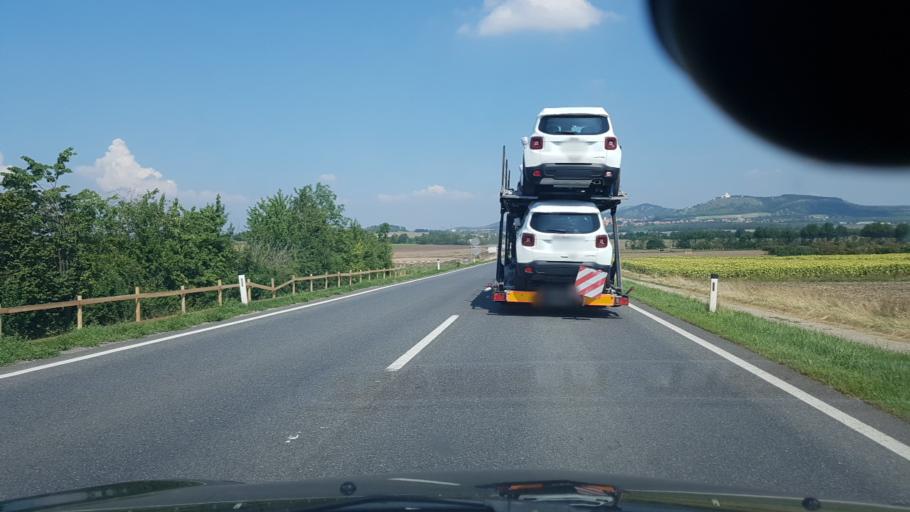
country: AT
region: Lower Austria
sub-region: Politischer Bezirk Mistelbach
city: Drasenhofen
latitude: 48.7703
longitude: 16.6431
